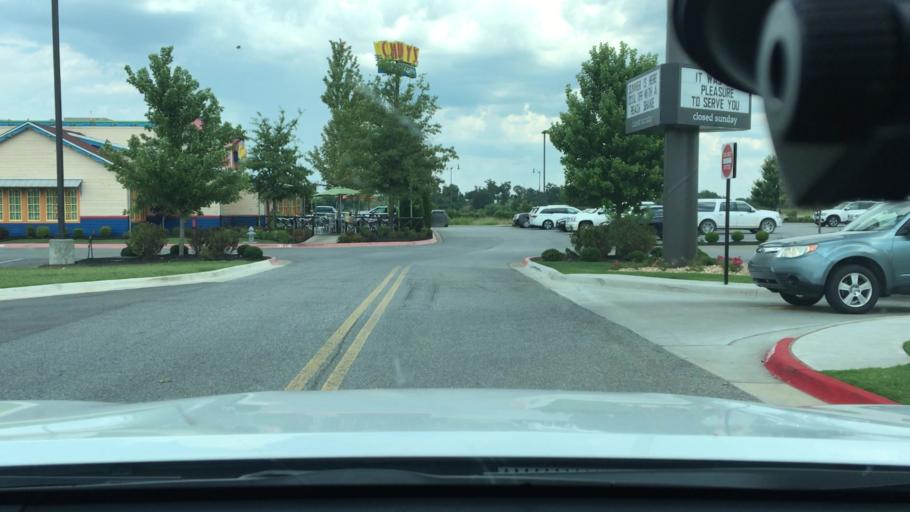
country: US
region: Arkansas
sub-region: Benton County
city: Cave Springs
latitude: 36.2982
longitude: -94.1832
